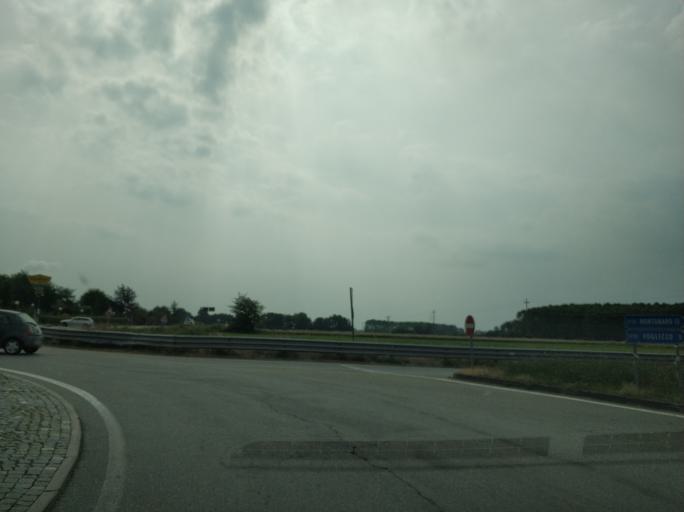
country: IT
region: Piedmont
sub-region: Provincia di Torino
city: San Giusto Canavese
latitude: 45.3157
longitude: 7.8287
